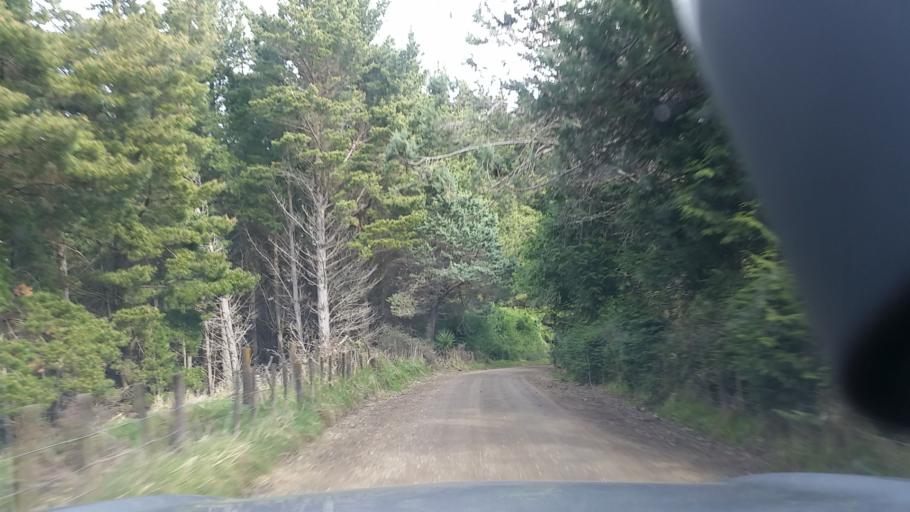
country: NZ
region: Hawke's Bay
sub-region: Napier City
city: Napier
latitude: -39.2295
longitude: 176.9946
